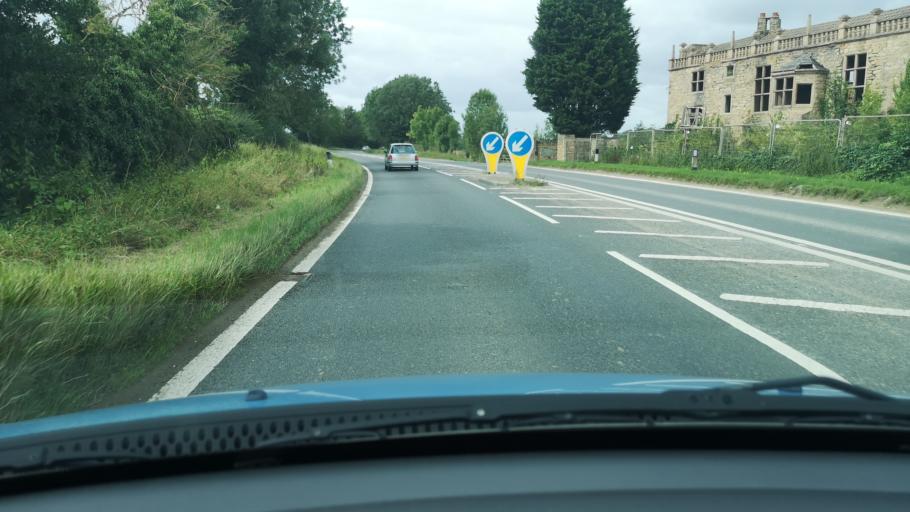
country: GB
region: England
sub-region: City and Borough of Wakefield
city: South Elmsall
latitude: 53.5861
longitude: -1.2377
